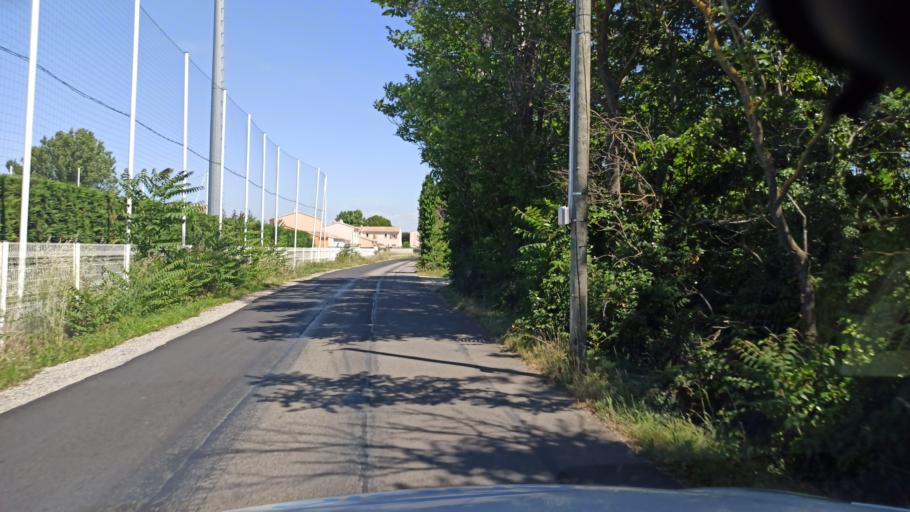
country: FR
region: Provence-Alpes-Cote d'Azur
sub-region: Departement du Vaucluse
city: Sorgues
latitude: 43.9947
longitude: 4.8806
